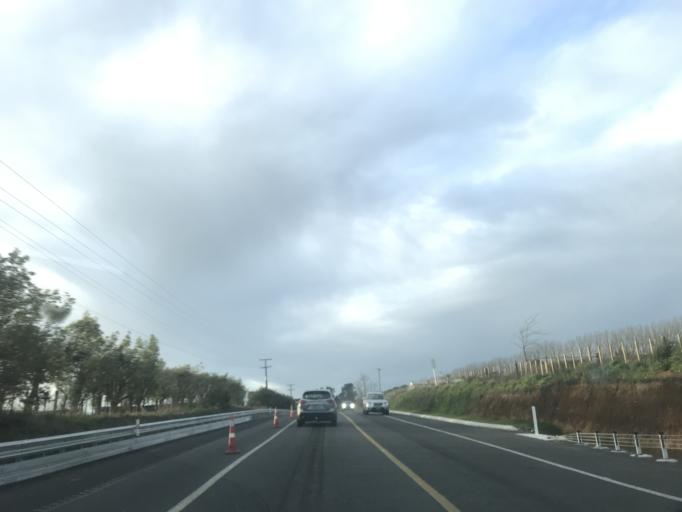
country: NZ
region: Bay of Plenty
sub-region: Western Bay of Plenty District
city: Waihi Beach
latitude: -37.4489
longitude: 175.8786
